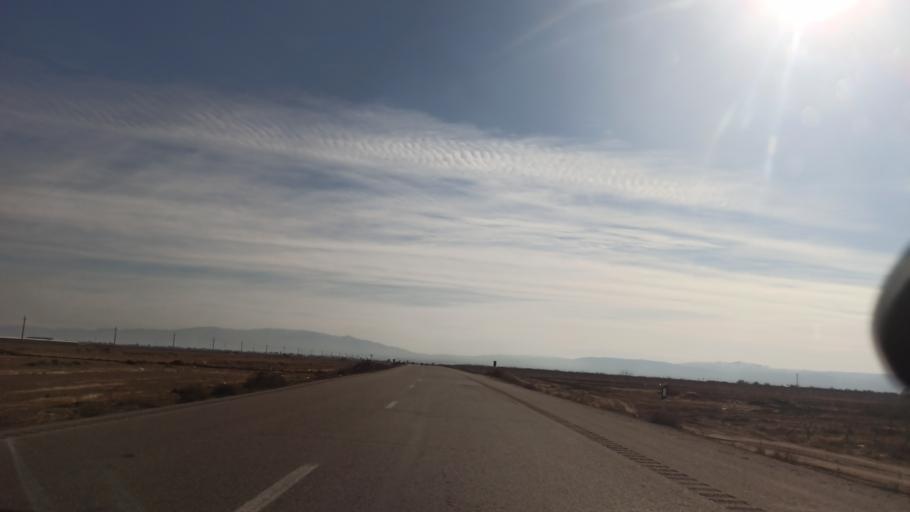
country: IR
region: Qazvin
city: Bu'in Zahra
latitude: 35.8123
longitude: 50.0759
